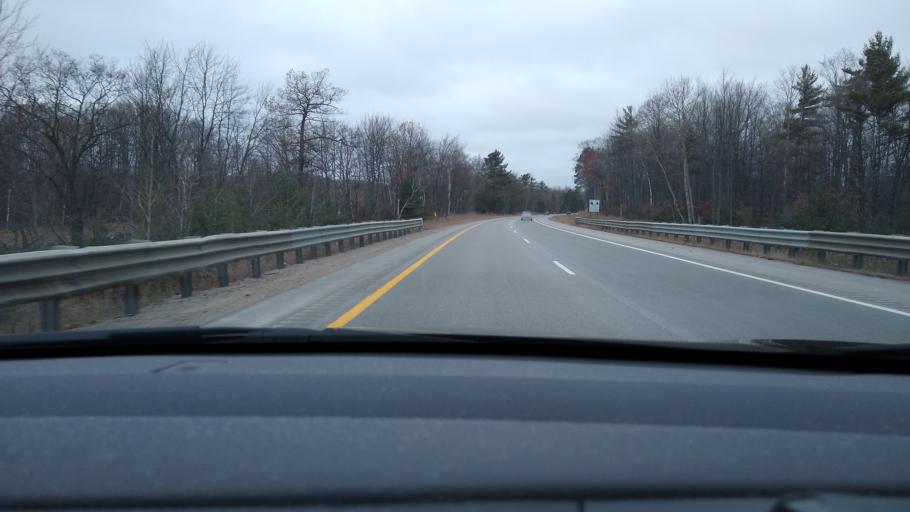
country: US
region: Michigan
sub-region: Otsego County
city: Gaylord
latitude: 44.9589
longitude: -84.6735
